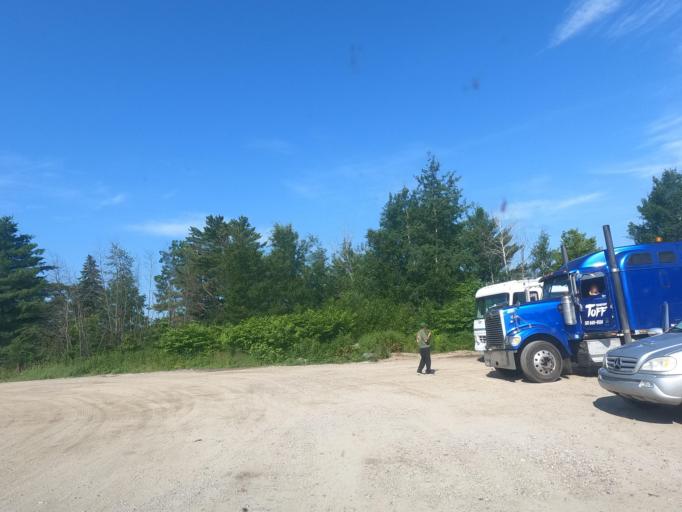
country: CA
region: Ontario
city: Mattawa
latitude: 46.3109
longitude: -78.7114
